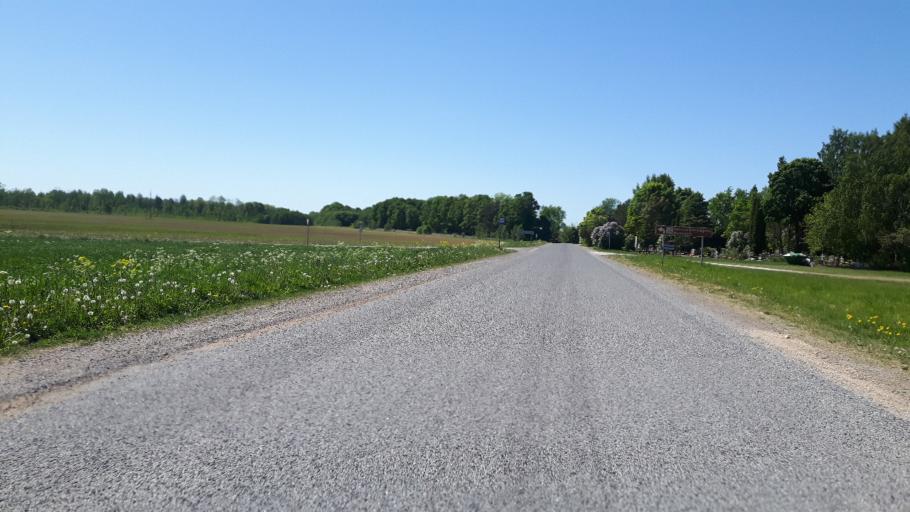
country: EE
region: Ida-Virumaa
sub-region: Sillamaee linn
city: Sillamae
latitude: 59.3731
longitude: 27.8506
